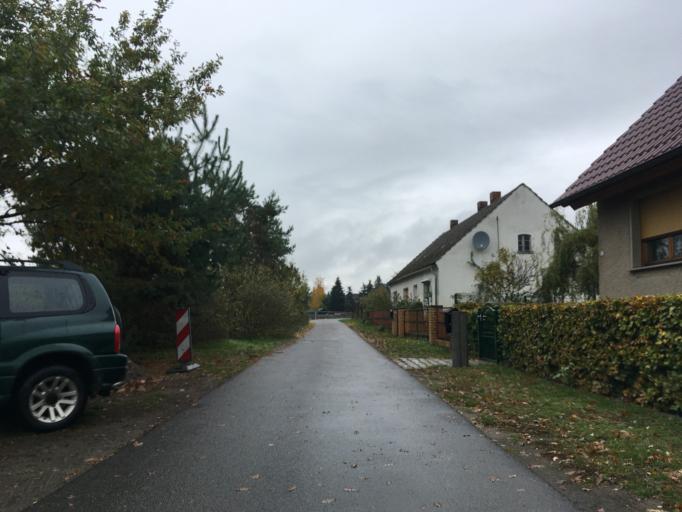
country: DE
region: Brandenburg
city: Friedland
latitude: 52.0379
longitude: 14.1789
